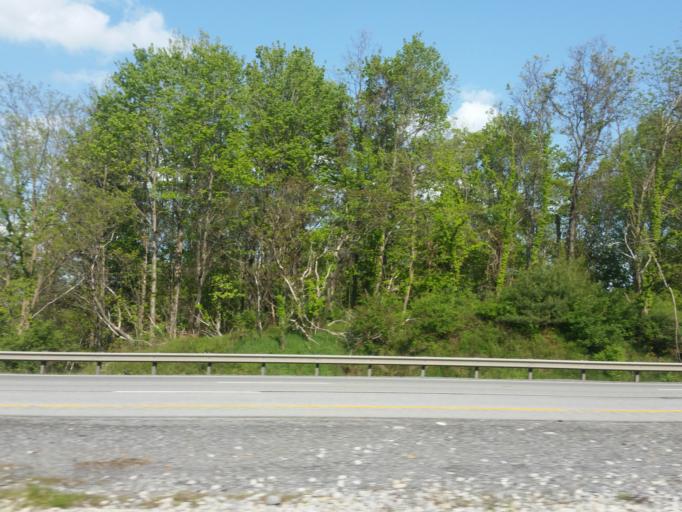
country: US
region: West Virginia
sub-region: Raleigh County
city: Shady Spring
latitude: 37.5526
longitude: -81.1138
